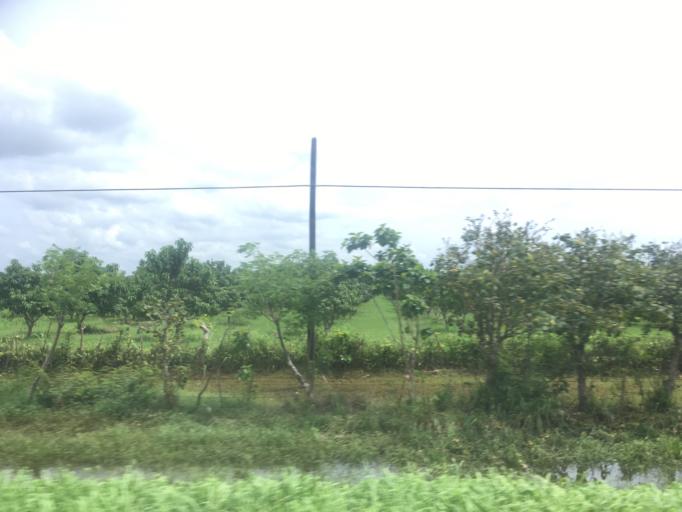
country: CU
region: Matanzas
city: Jovellanos
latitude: 22.7978
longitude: -81.1575
